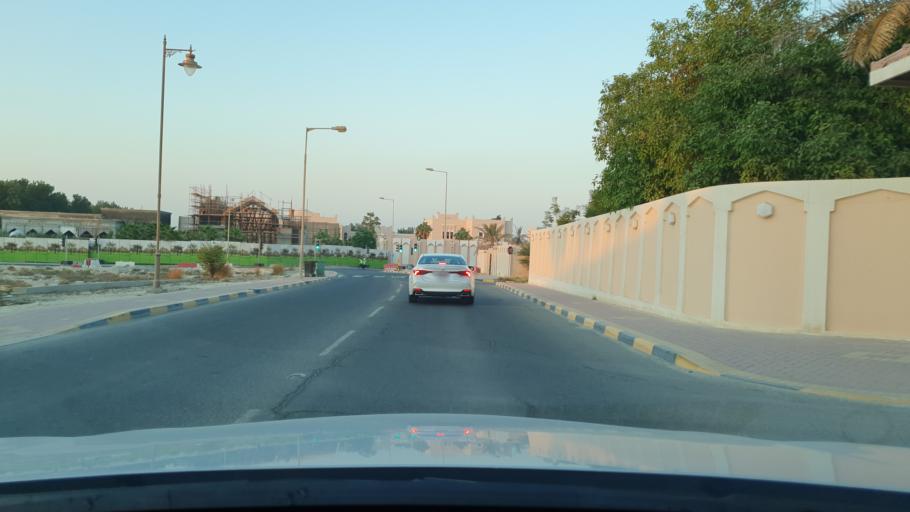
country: BH
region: Northern
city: Ar Rifa'
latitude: 26.1396
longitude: 50.5328
